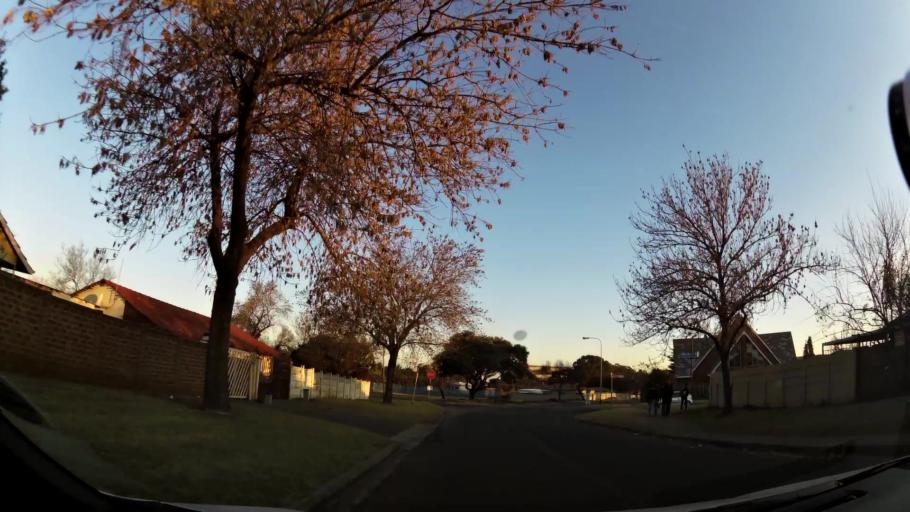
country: ZA
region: Gauteng
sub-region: Ekurhuleni Metropolitan Municipality
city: Germiston
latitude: -26.2700
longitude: 28.1617
